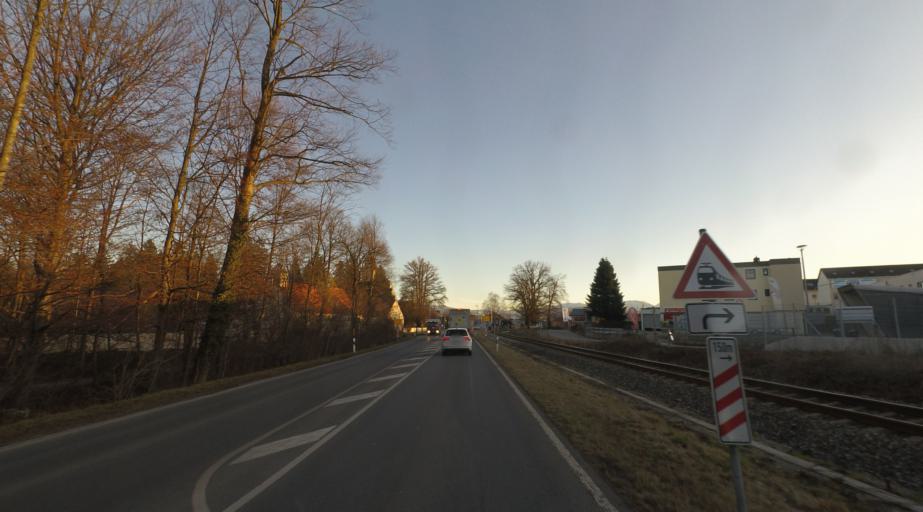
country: DE
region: Bavaria
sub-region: Upper Bavaria
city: Traunstein
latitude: 47.8850
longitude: 12.6321
